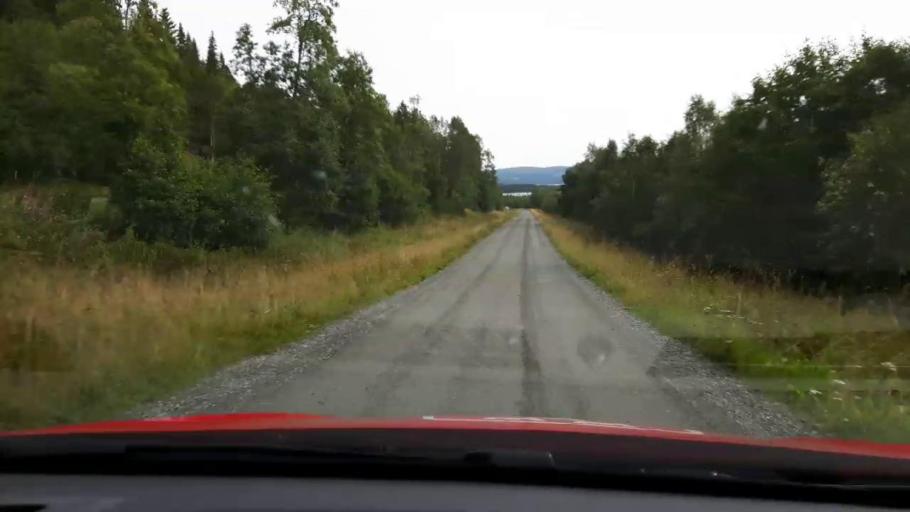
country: SE
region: Jaemtland
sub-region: Are Kommun
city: Are
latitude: 63.7468
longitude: 12.9704
